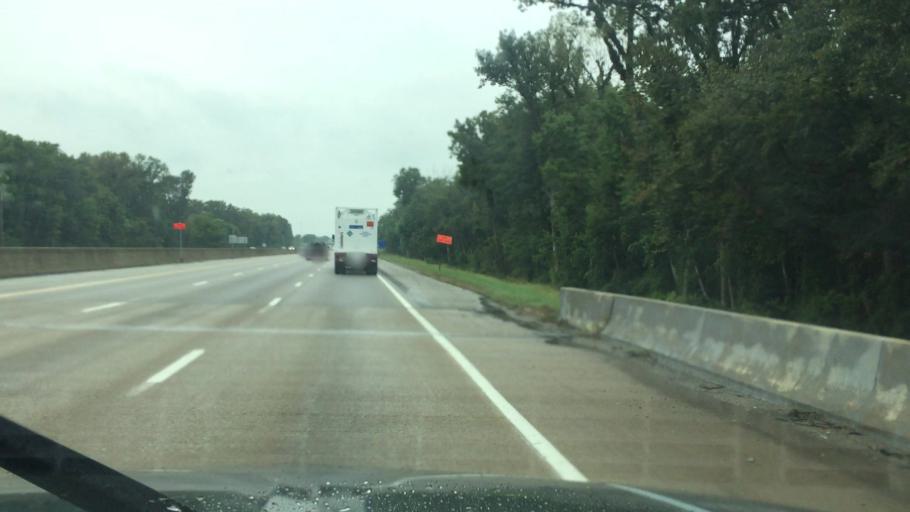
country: US
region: Ohio
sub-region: Clark County
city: Crystal Lakes
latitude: 39.8647
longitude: -84.0197
